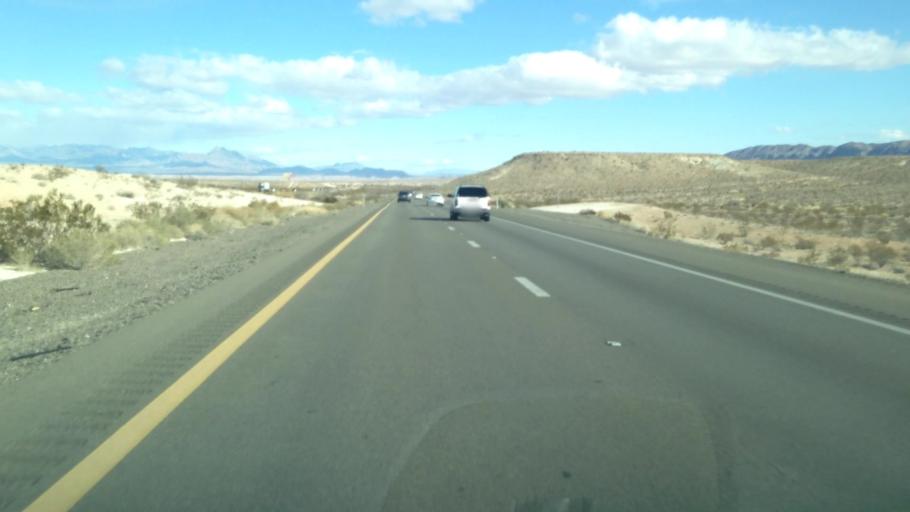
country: US
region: Nevada
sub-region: Clark County
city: Moapa Town
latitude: 36.5365
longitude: -114.7171
